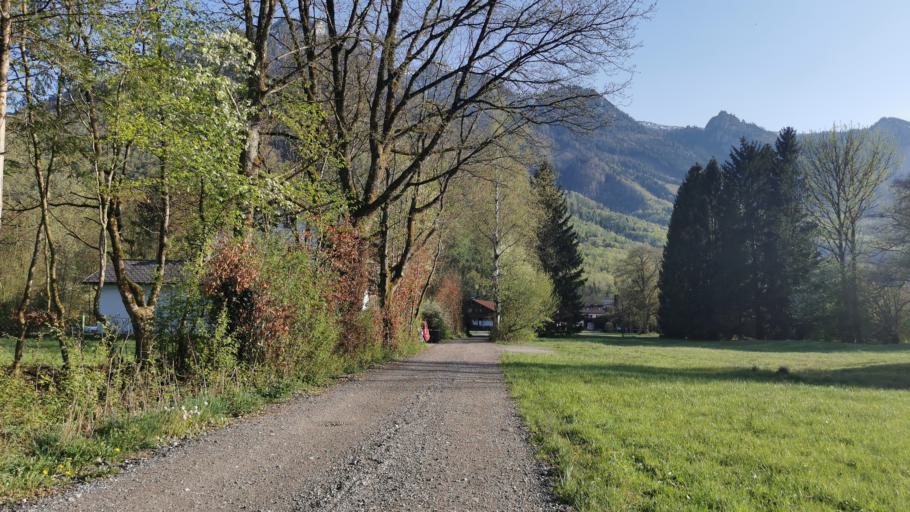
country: AT
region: Salzburg
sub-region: Politischer Bezirk Salzburg-Umgebung
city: Grodig
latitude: 47.7504
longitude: 13.0001
